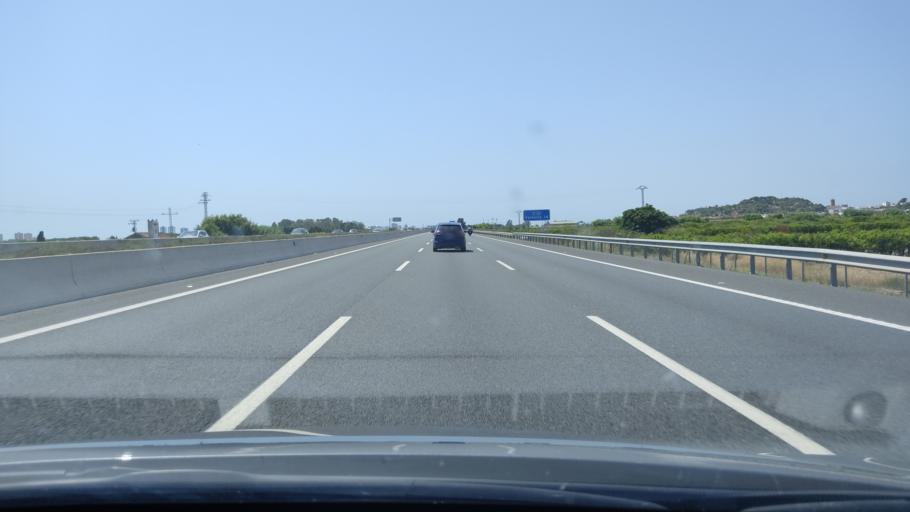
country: ES
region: Valencia
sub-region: Provincia de Valencia
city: Pucol
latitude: 39.6039
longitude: -0.2939
